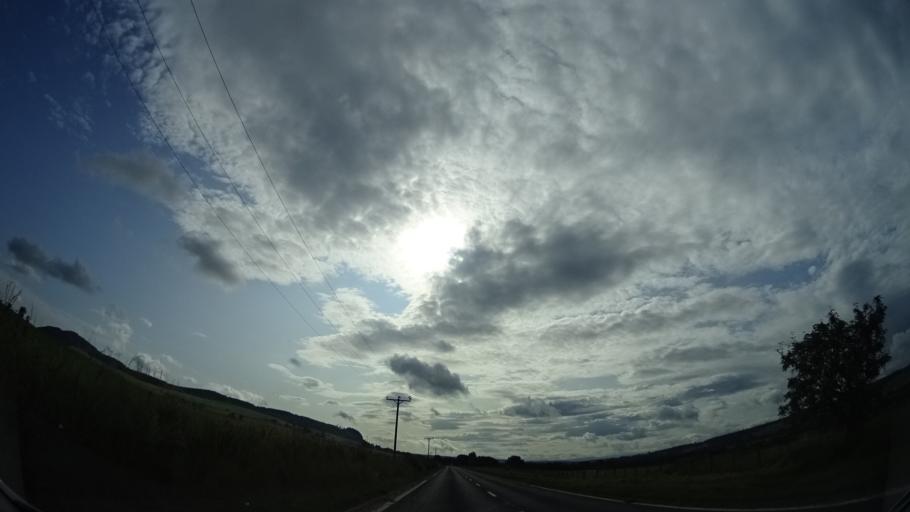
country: GB
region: Scotland
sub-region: Highland
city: Muir of Ord
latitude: 57.5622
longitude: -4.5690
